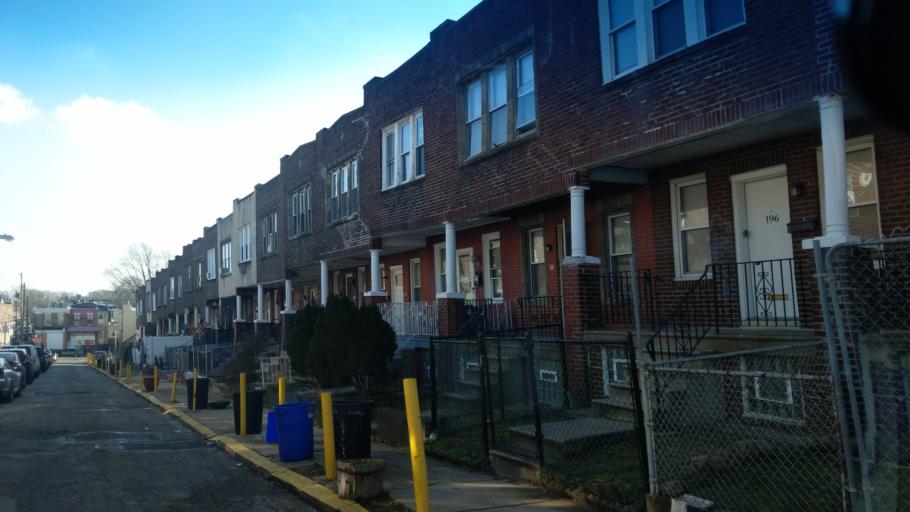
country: US
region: Pennsylvania
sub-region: Montgomery County
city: Rockledge
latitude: 40.0210
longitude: -75.1278
